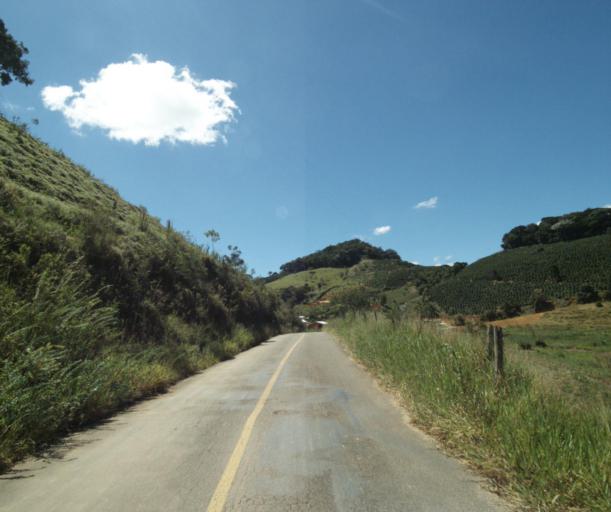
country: BR
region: Minas Gerais
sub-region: Espera Feliz
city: Espera Feliz
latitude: -20.6376
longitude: -41.8127
